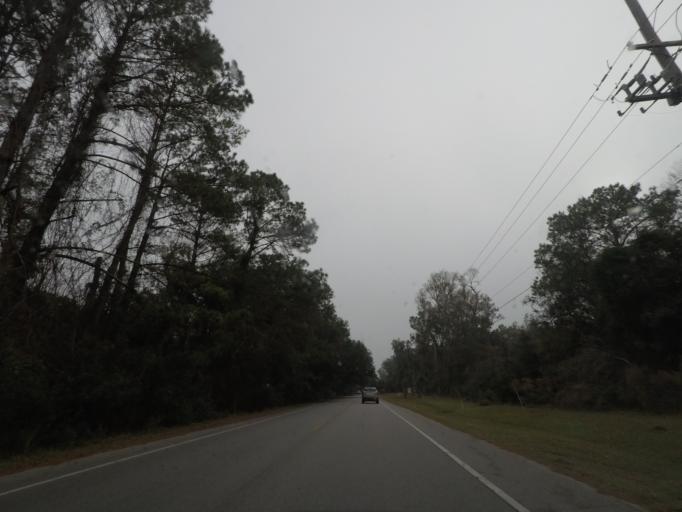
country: US
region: South Carolina
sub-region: Charleston County
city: Seabrook Island
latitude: 32.5146
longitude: -80.2997
